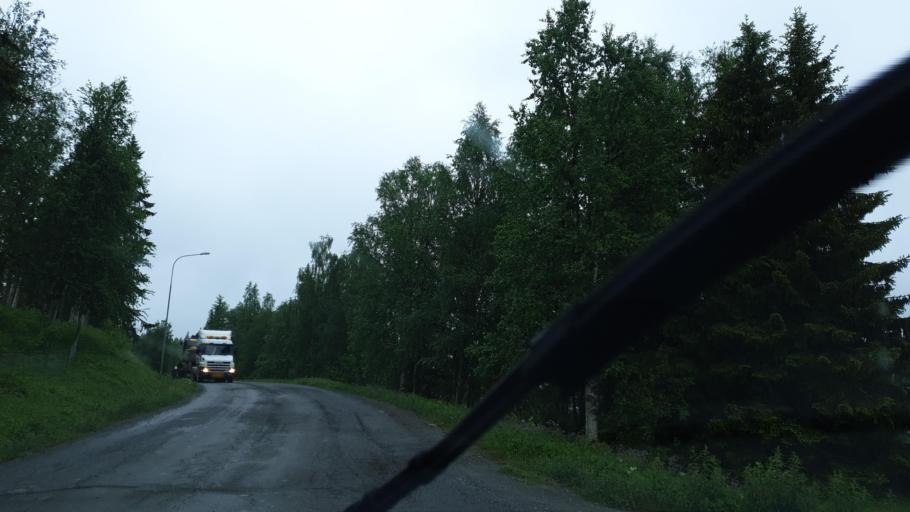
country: SE
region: Vaesterbotten
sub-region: Vilhelmina Kommun
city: Sjoberg
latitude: 65.2368
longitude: 15.9933
